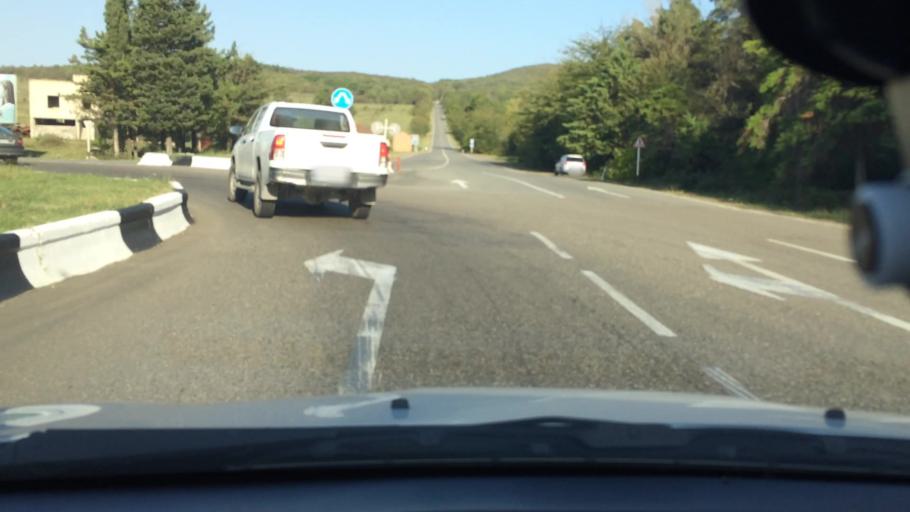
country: GE
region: Imereti
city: Kutaisi
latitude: 42.2397
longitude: 42.7662
